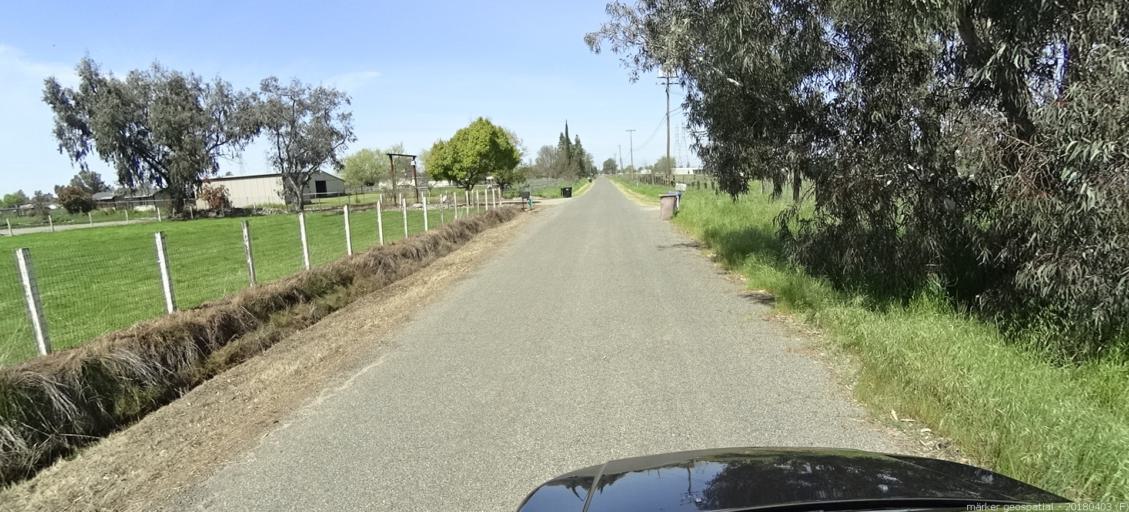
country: US
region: California
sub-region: Sacramento County
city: Clay
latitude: 38.3475
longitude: -121.2146
